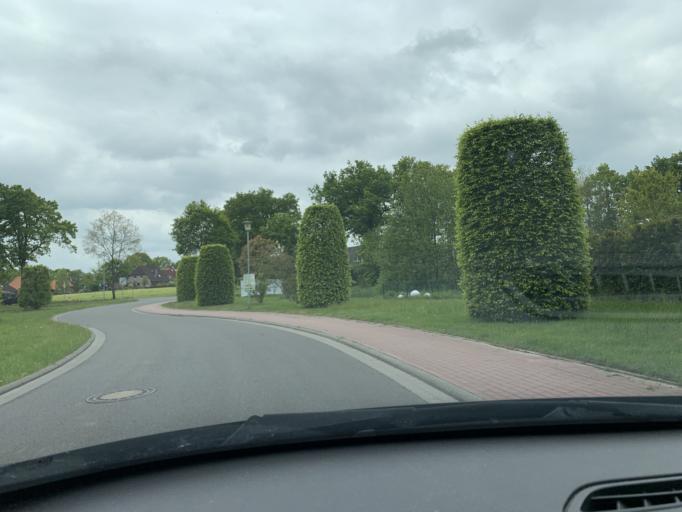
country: DE
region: Lower Saxony
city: Westerstede
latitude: 53.2495
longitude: 7.9084
